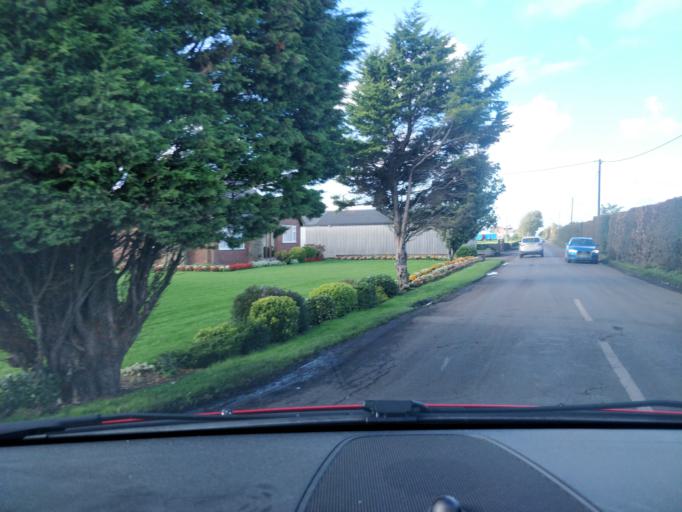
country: GB
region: England
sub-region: Lancashire
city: Tarleton
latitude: 53.6738
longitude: -2.8674
